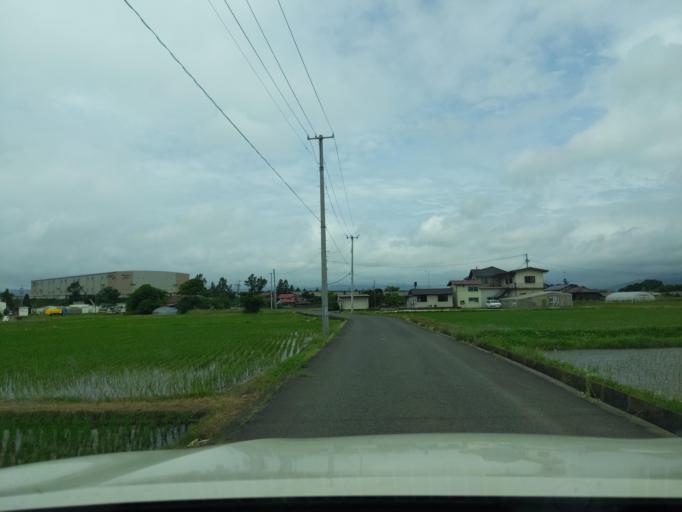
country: JP
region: Fukushima
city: Koriyama
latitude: 37.4376
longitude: 140.3517
